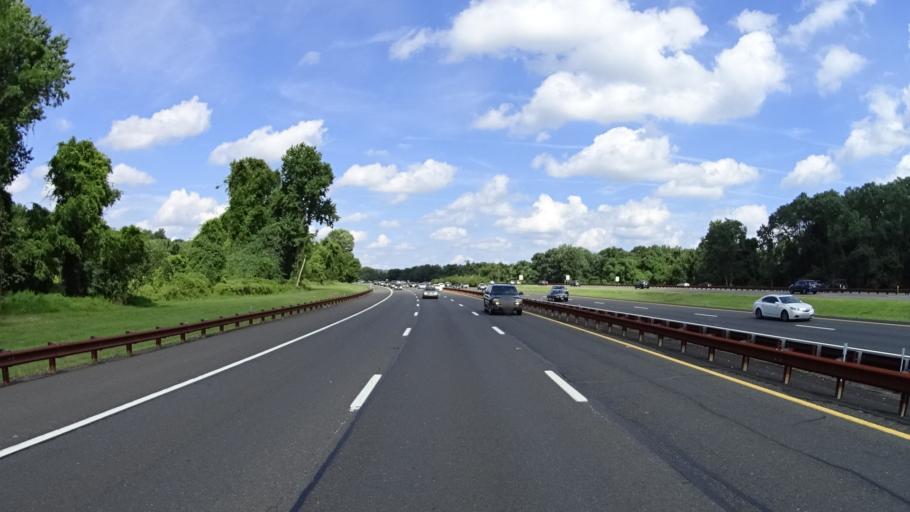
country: US
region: New Jersey
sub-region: Monmouth County
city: Lincroft
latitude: 40.3513
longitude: -74.1185
